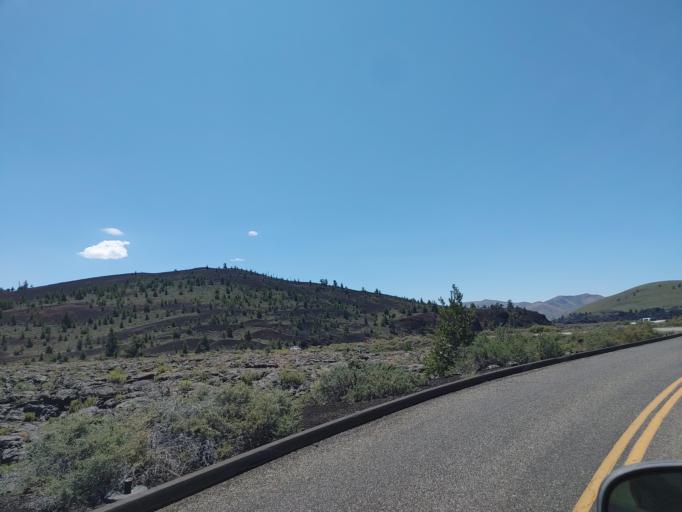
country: US
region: Idaho
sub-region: Butte County
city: Arco
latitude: 43.4578
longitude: -113.5575
